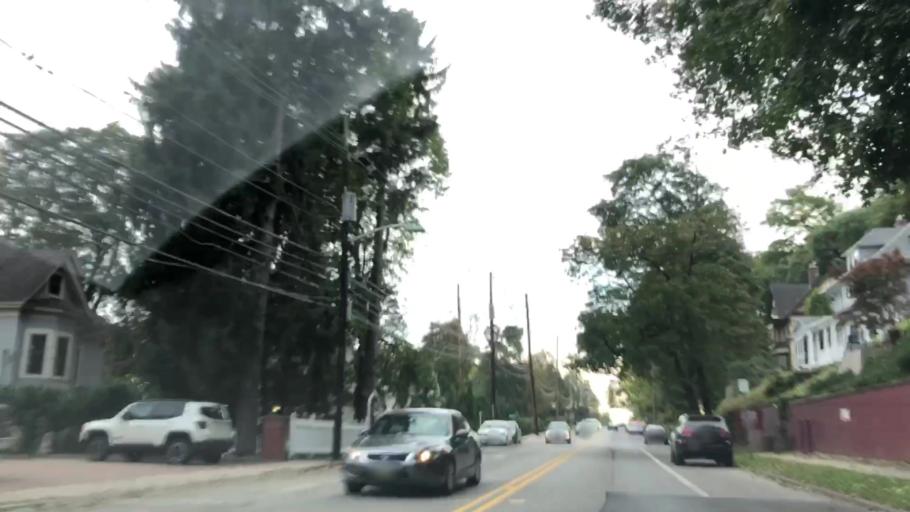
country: US
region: New Jersey
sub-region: Essex County
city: Upper Montclair
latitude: 40.8595
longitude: -74.1962
